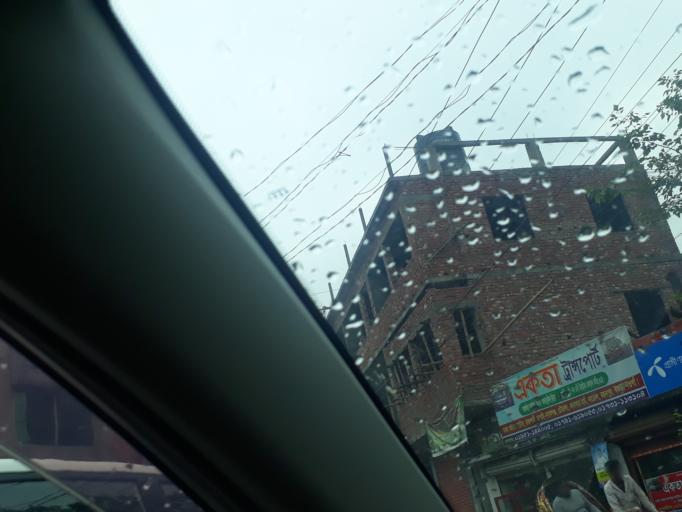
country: BD
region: Dhaka
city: Tungi
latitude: 23.8977
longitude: 90.3307
